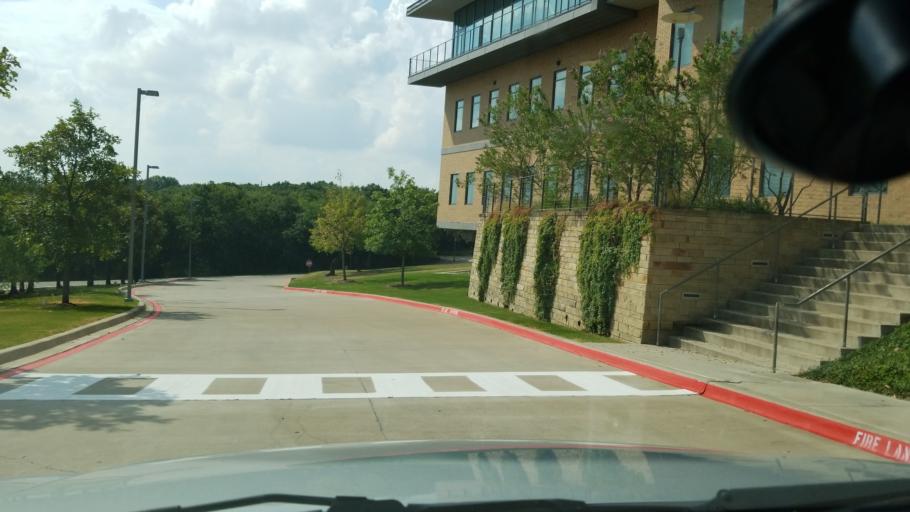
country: US
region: Texas
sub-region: Dallas County
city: Irving
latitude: 32.8483
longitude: -96.9204
